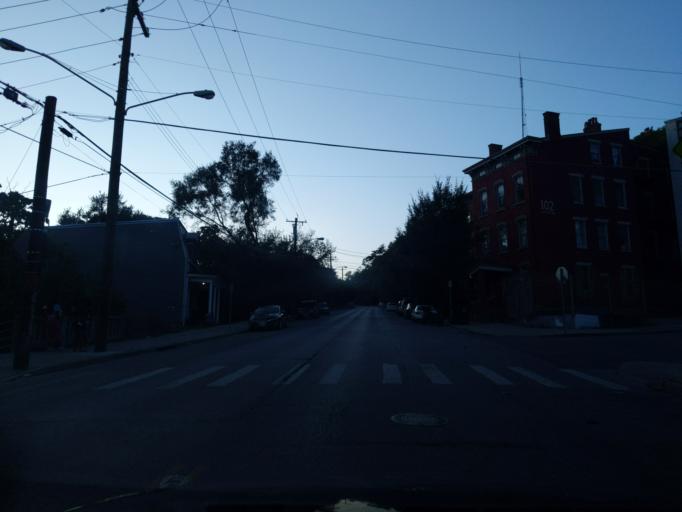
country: US
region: Kentucky
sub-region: Campbell County
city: Newport
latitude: 39.1190
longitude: -84.5180
